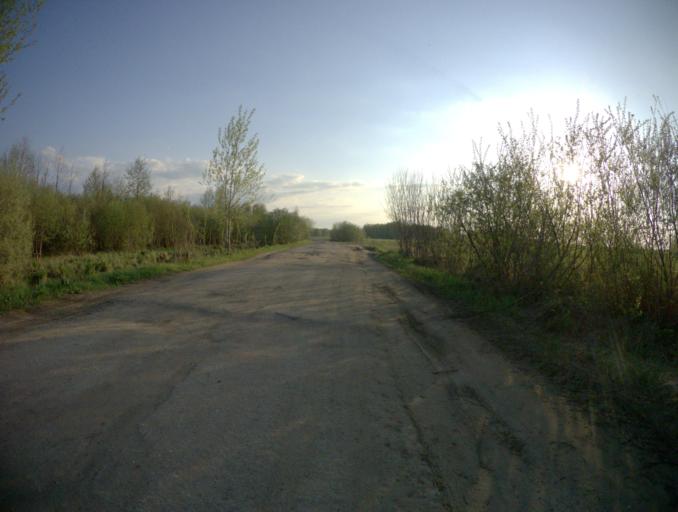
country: RU
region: Vladimir
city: Vyazniki
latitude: 56.3179
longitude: 42.1026
